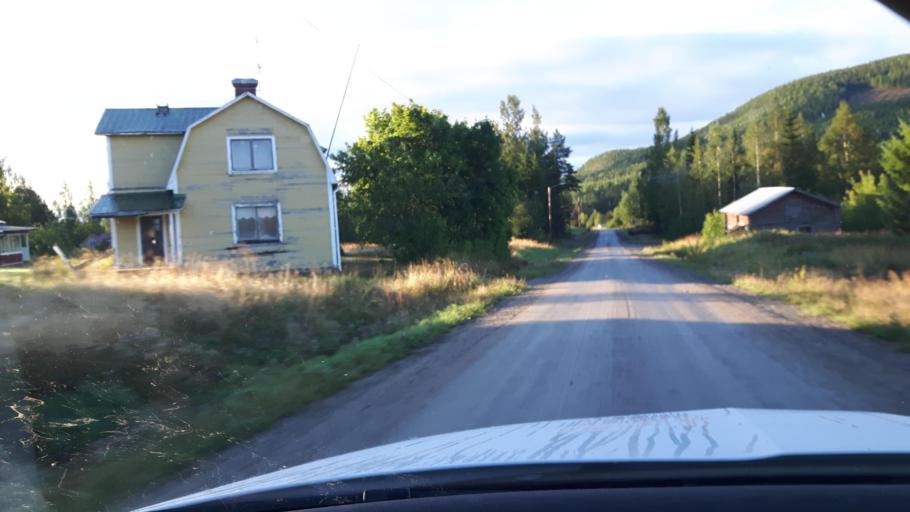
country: SE
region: Gaevleborg
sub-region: Ljusdals Kommun
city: Farila
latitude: 62.0694
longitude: 15.7804
